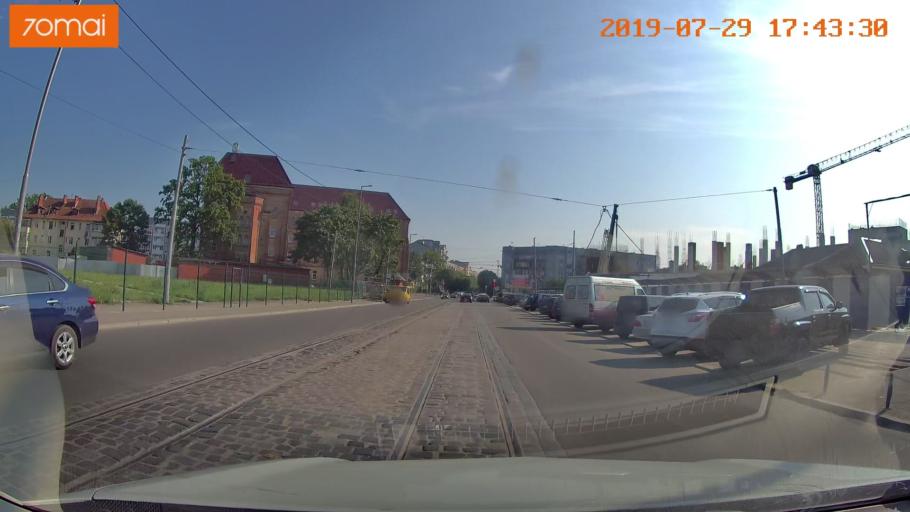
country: RU
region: Kaliningrad
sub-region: Gorod Kaliningrad
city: Kaliningrad
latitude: 54.7224
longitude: 20.5144
